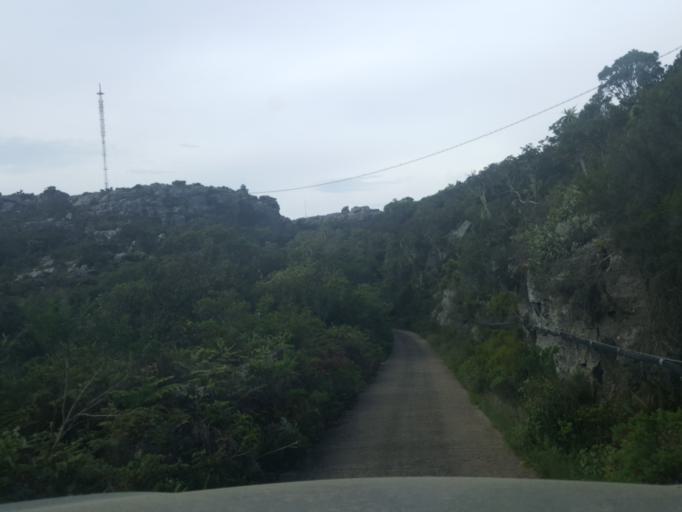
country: ZA
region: Limpopo
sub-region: Mopani District Municipality
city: Hoedspruit
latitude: -24.5488
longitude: 30.8691
